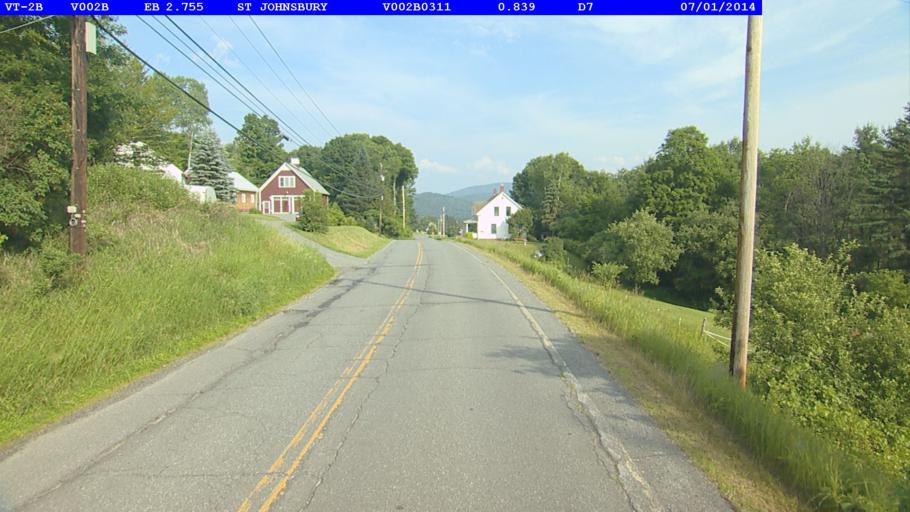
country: US
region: Vermont
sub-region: Caledonia County
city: St Johnsbury
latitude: 44.4250
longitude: -72.0411
